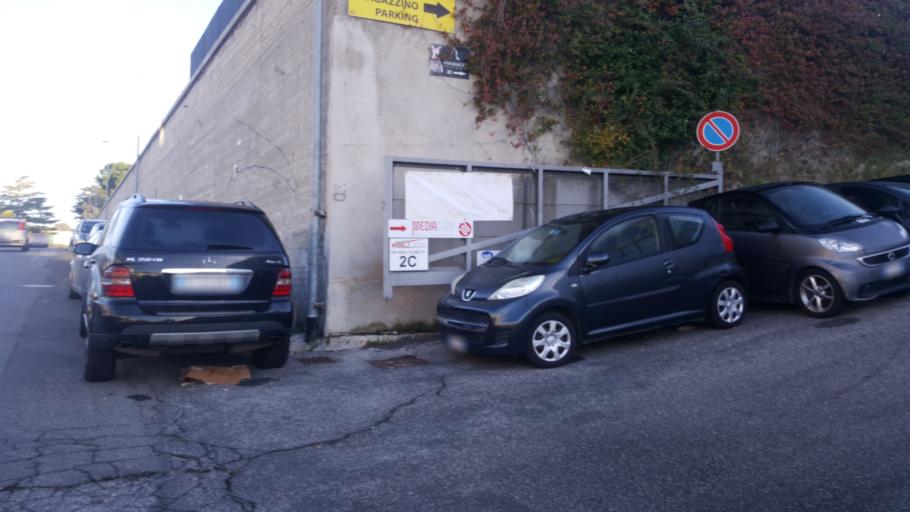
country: IT
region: Latium
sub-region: Citta metropolitana di Roma Capitale
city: Formello
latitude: 42.0504
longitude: 12.4031
